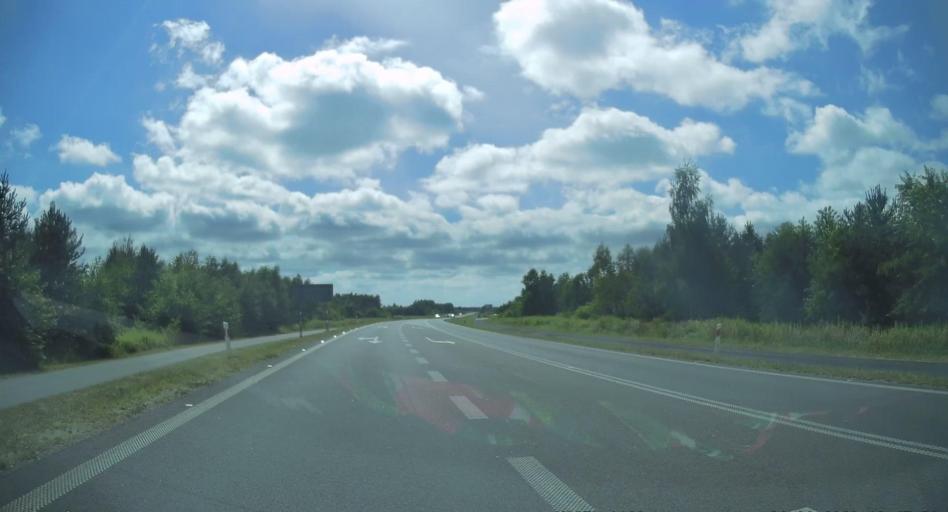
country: PL
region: Subcarpathian Voivodeship
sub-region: Powiat mielecki
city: Padew Narodowa
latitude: 50.3513
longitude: 21.4935
